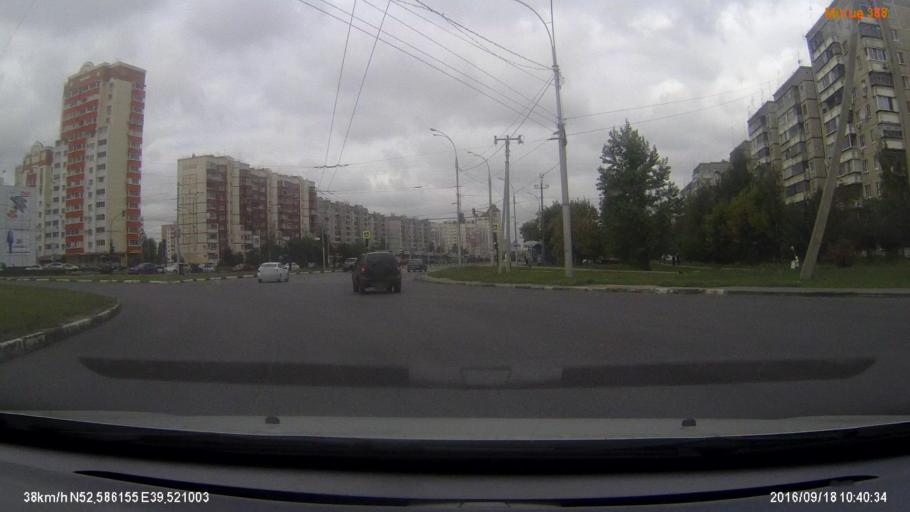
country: RU
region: Lipetsk
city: Syrskoye
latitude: 52.5859
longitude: 39.5210
